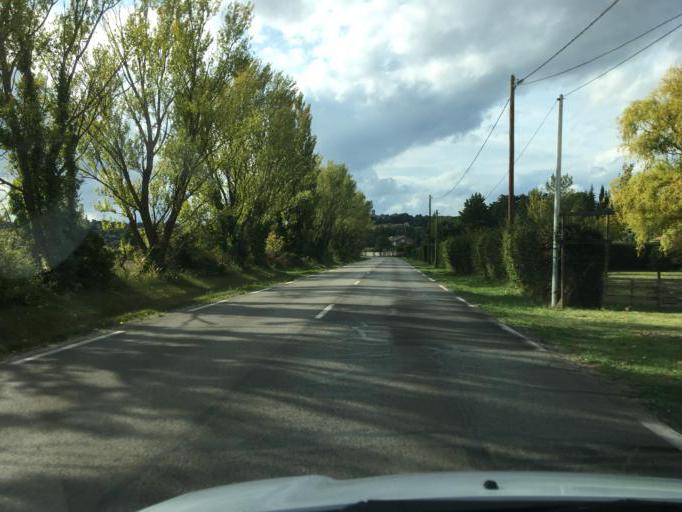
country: FR
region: Provence-Alpes-Cote d'Azur
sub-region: Departement du Vaucluse
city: Chateauneuf-de-Gadagne
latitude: 43.9262
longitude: 4.9570
